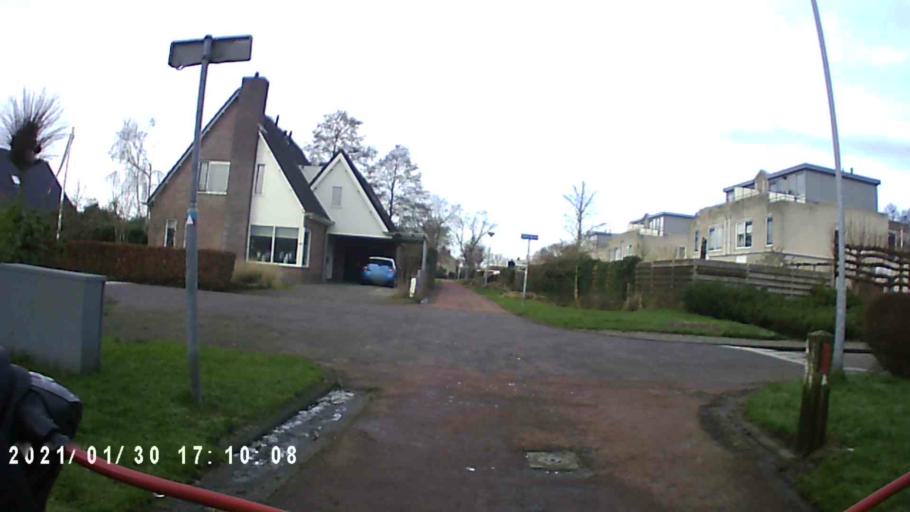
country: NL
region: Groningen
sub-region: Gemeente Leek
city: Leek
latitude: 53.1672
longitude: 6.3641
